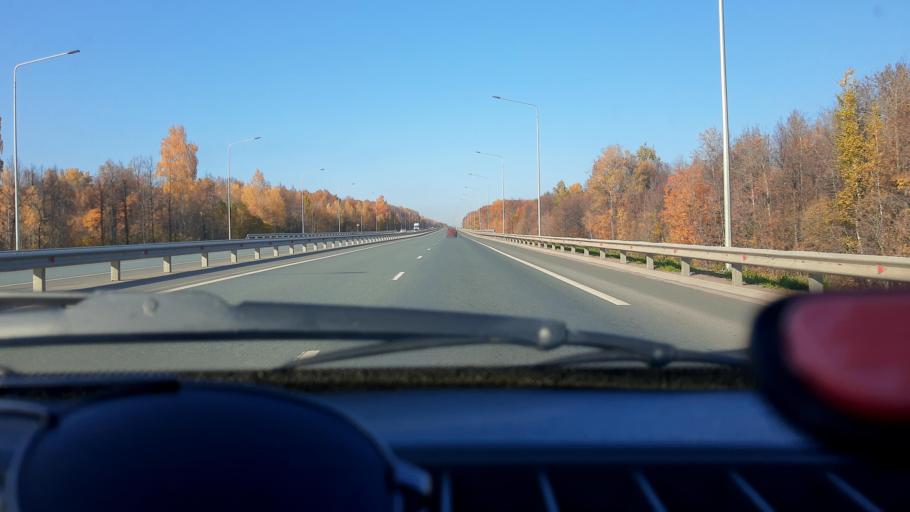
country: RU
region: Bashkortostan
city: Karmaskaly
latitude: 54.3880
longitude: 55.9178
